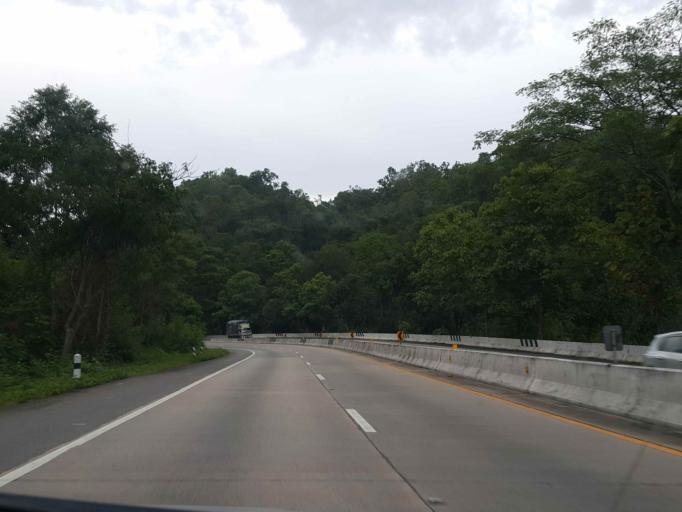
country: TH
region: Lamphun
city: Mae Tha
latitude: 18.3992
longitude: 99.2142
